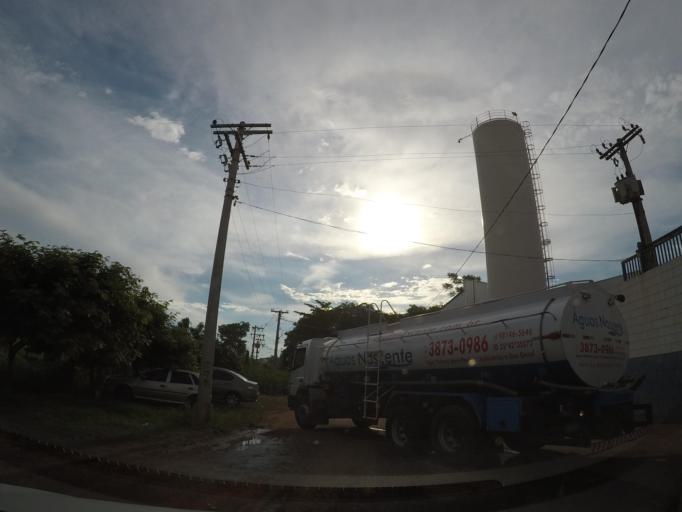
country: BR
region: Sao Paulo
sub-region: Sumare
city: Sumare
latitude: -22.8240
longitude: -47.2544
